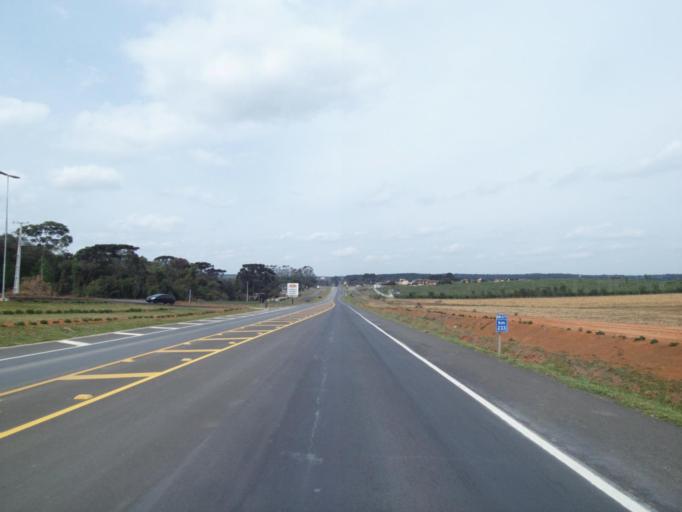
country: BR
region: Parana
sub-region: Irati
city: Irati
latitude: -25.4643
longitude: -50.5668
